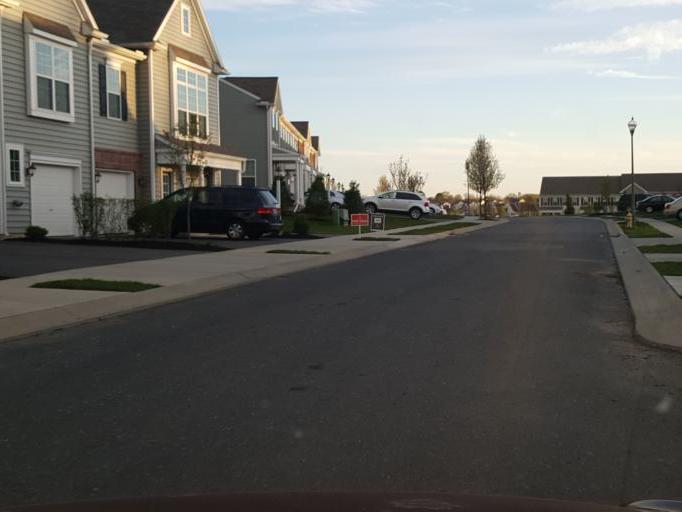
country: US
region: Pennsylvania
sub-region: Dauphin County
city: Hummelstown
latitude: 40.2488
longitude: -76.7161
